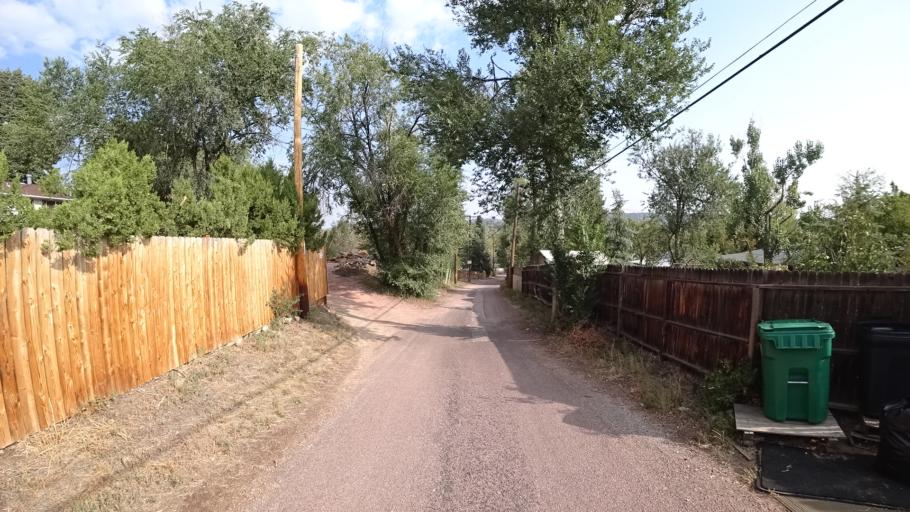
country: US
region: Colorado
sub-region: El Paso County
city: Colorado Springs
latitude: 38.8504
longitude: -104.7866
